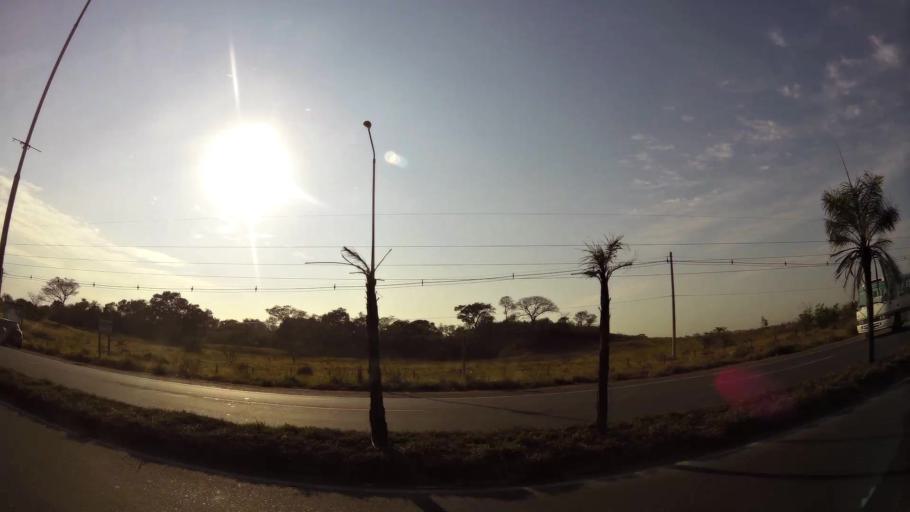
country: BO
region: Santa Cruz
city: Santa Cruz de la Sierra
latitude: -17.6622
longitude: -63.1582
